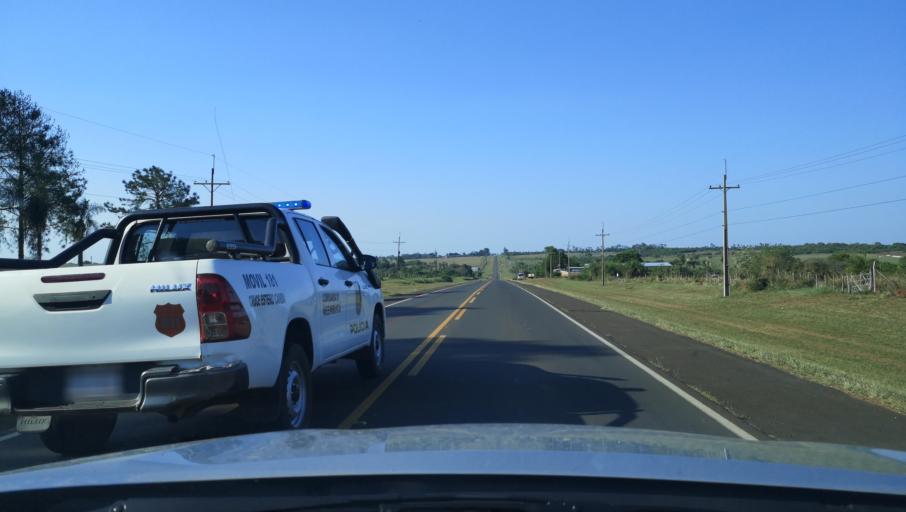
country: PY
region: Misiones
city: Santa Maria
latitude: -26.8394
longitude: -57.0355
